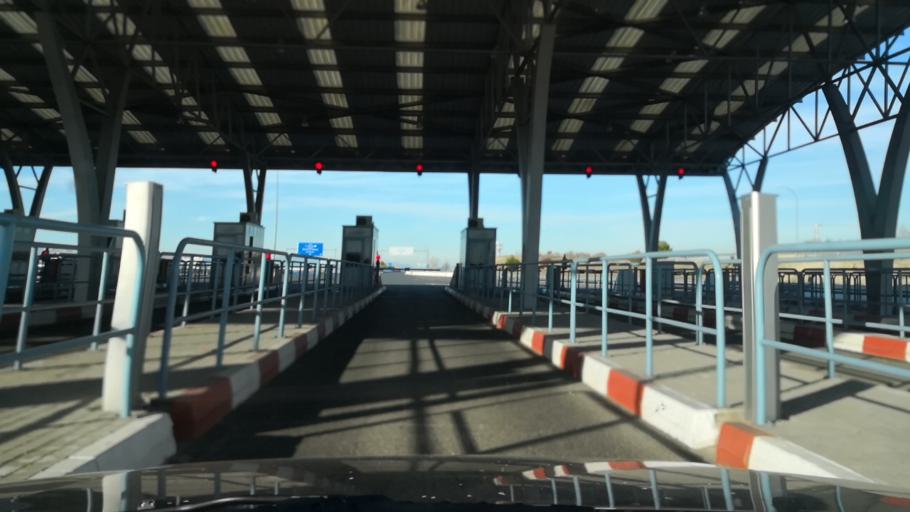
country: ES
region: Madrid
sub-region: Provincia de Madrid
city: Barajas de Madrid
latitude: 40.4771
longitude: -3.6012
